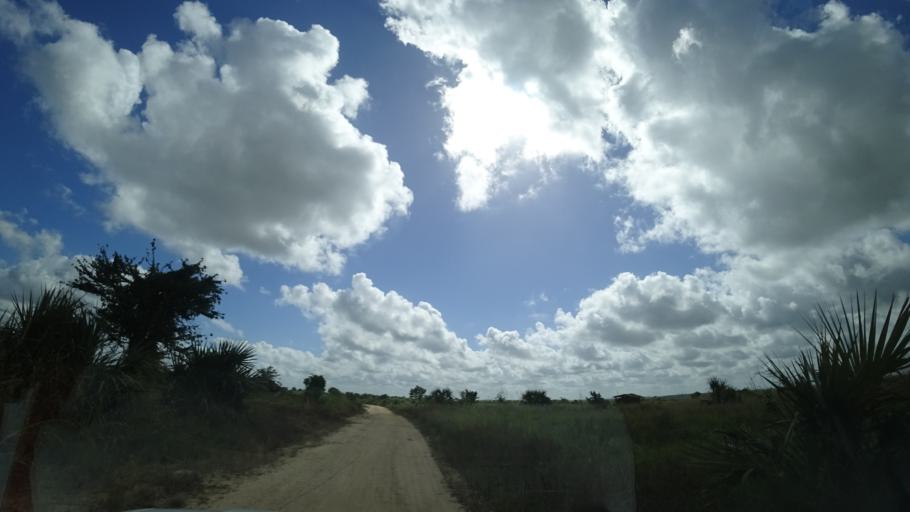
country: MZ
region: Sofala
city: Dondo
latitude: -19.4138
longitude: 34.5664
